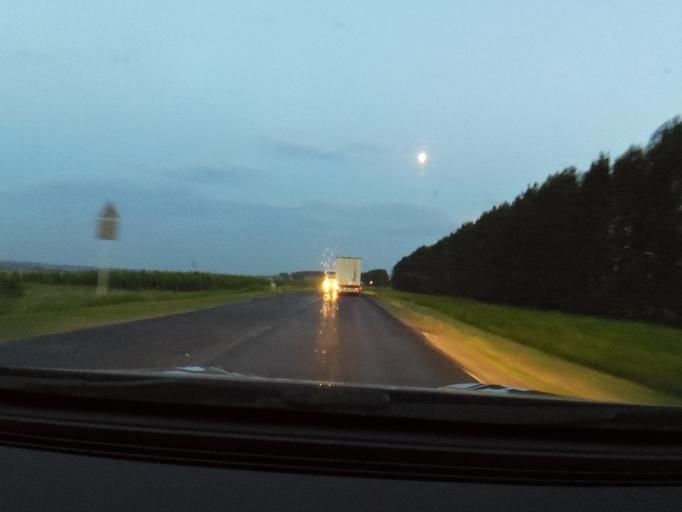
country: RU
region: Bashkortostan
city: Duvan
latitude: 56.0648
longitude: 58.1884
